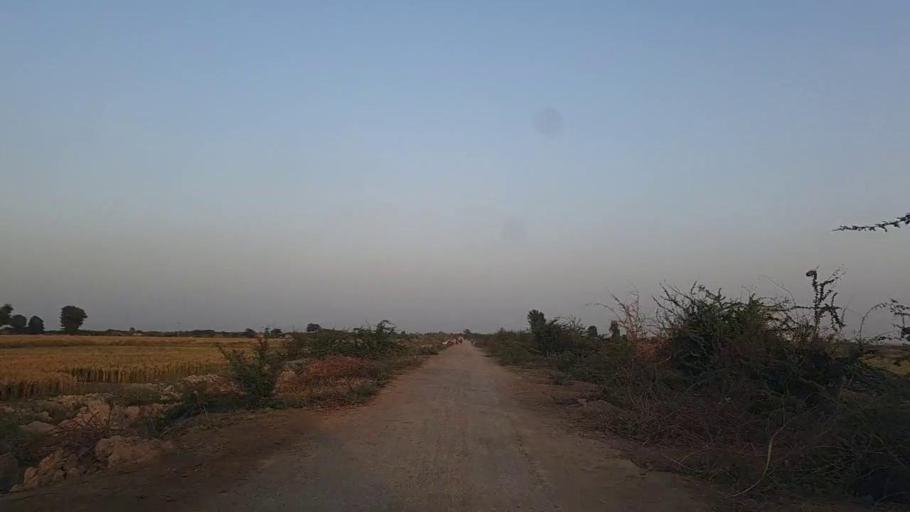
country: PK
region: Sindh
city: Naukot
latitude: 24.6952
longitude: 69.2786
